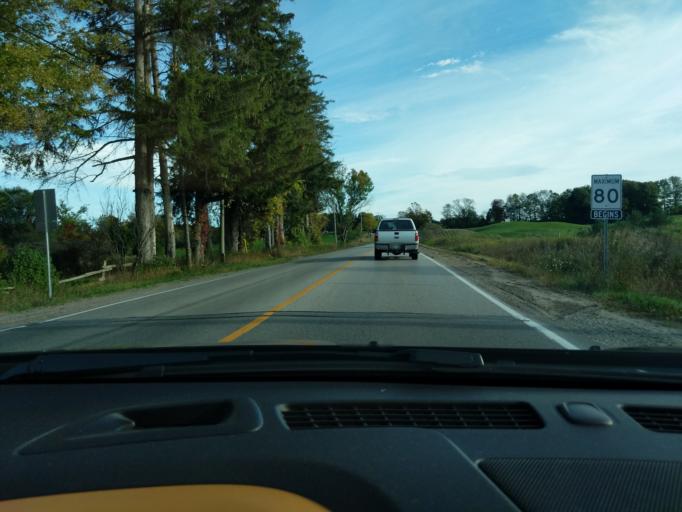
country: CA
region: Ontario
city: Barrie
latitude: 44.4234
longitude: -79.7613
